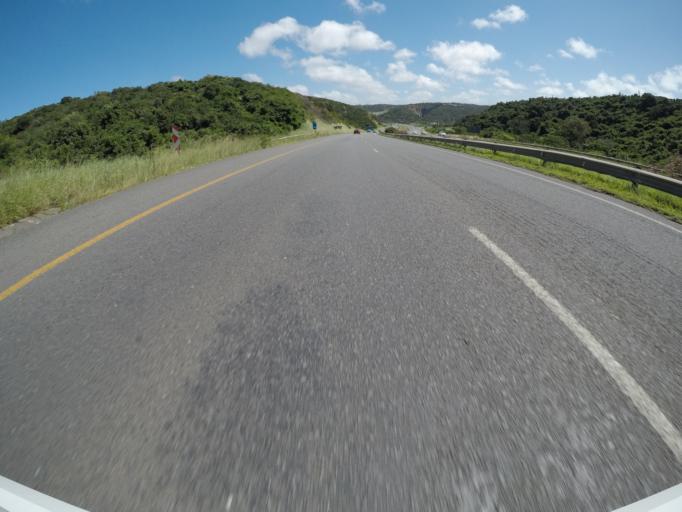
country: ZA
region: Eastern Cape
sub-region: Buffalo City Metropolitan Municipality
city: East London
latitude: -32.9600
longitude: 27.9263
